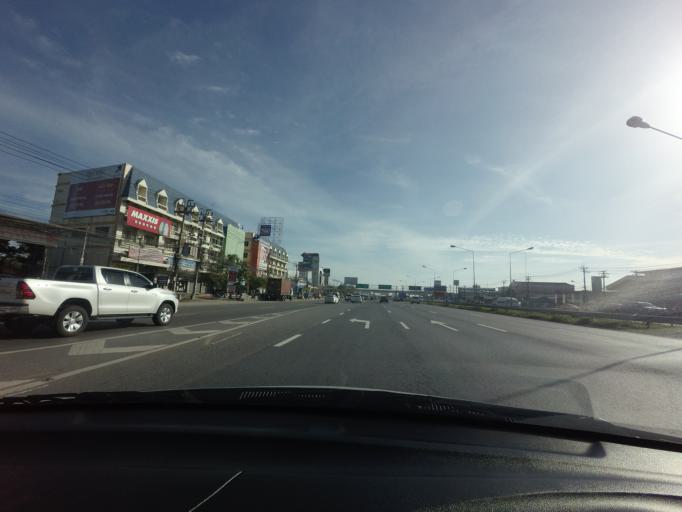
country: TH
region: Nonthaburi
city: Bang Bua Thong
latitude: 13.9307
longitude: 100.4148
